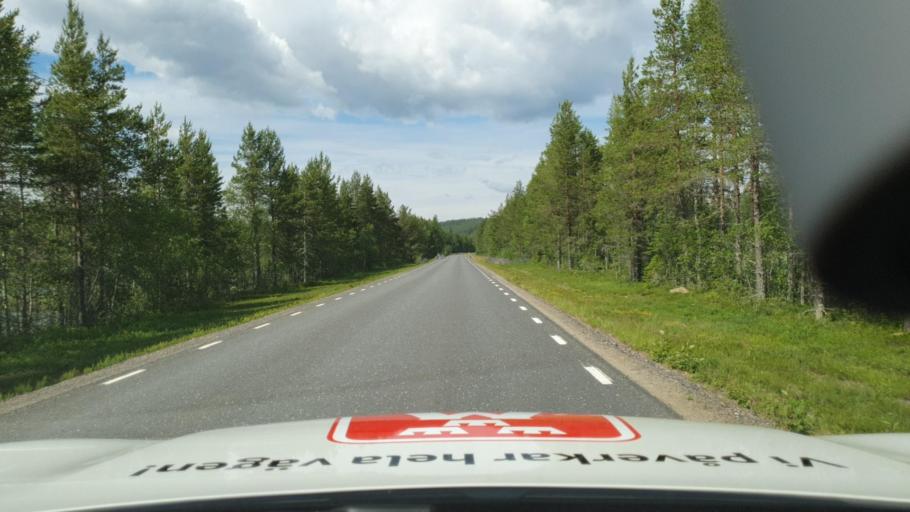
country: SE
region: Vaermland
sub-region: Torsby Kommun
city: Torsby
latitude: 60.6249
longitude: 12.7031
